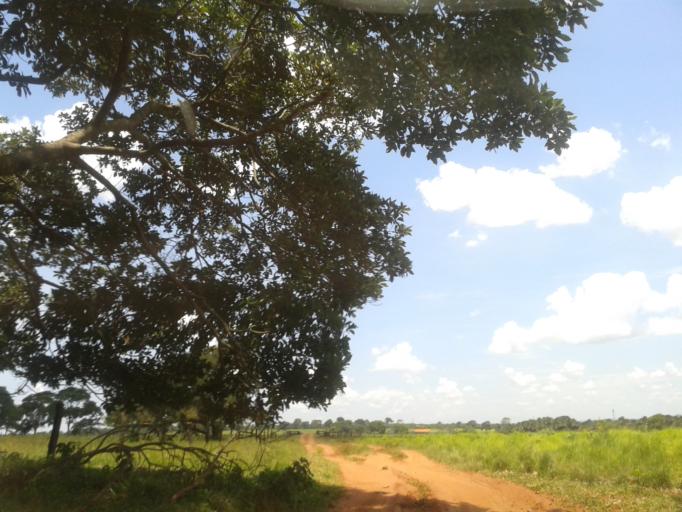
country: BR
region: Minas Gerais
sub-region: Santa Vitoria
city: Santa Vitoria
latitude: -19.2129
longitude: -50.4098
